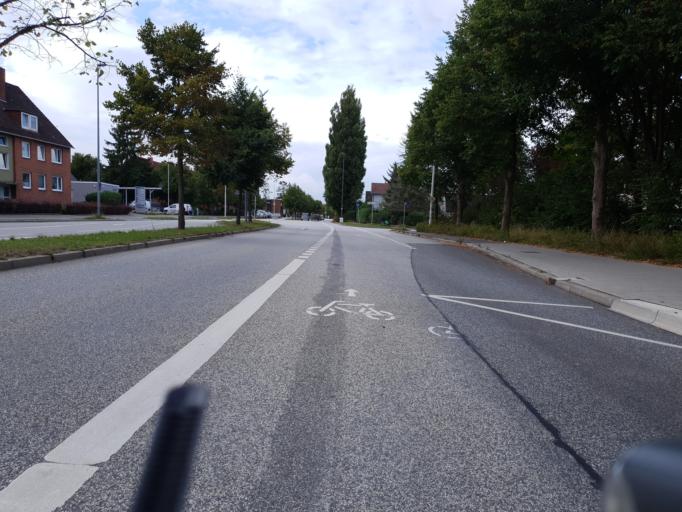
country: DE
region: Schleswig-Holstein
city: Kronshagen
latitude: 54.3536
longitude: 10.0886
